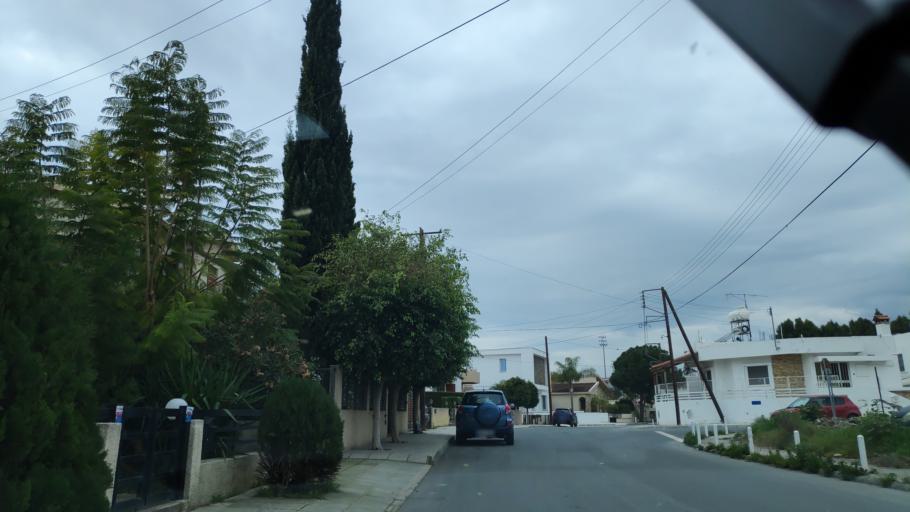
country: CY
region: Limassol
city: Limassol
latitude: 34.7003
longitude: 33.0280
